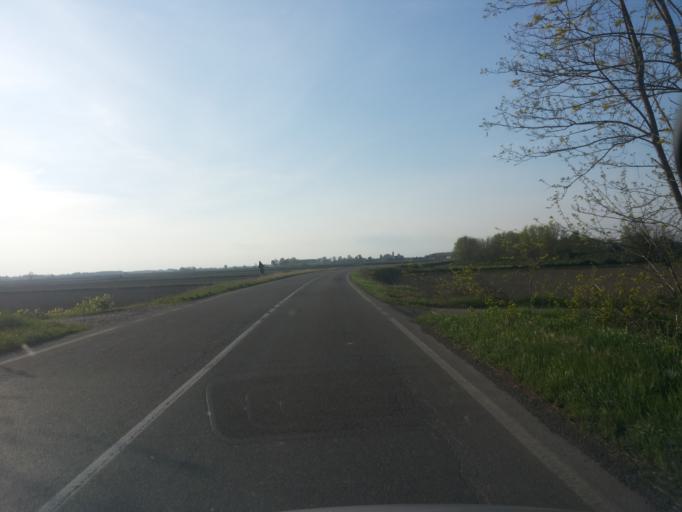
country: IT
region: Lombardy
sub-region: Provincia di Pavia
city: Langosco
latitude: 45.2006
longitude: 8.5815
